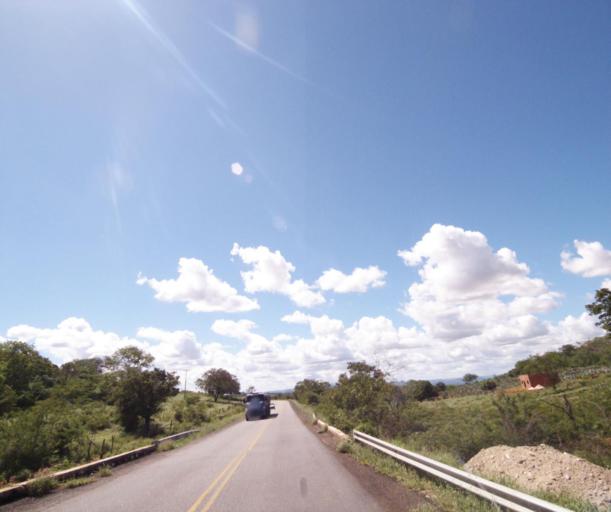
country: BR
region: Bahia
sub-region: Cacule
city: Cacule
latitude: -14.1949
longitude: -42.1418
